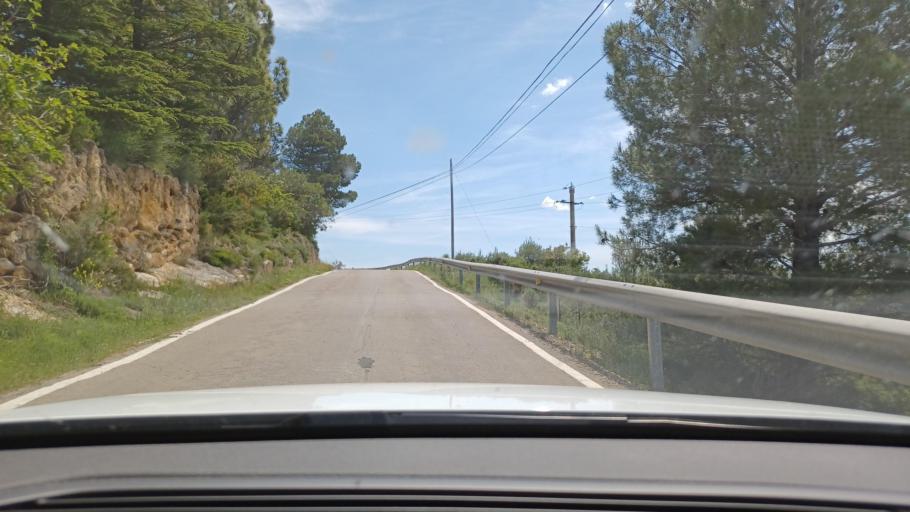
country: ES
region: Valencia
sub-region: Provincia de Castello
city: Rosell
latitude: 40.6459
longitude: 0.2697
